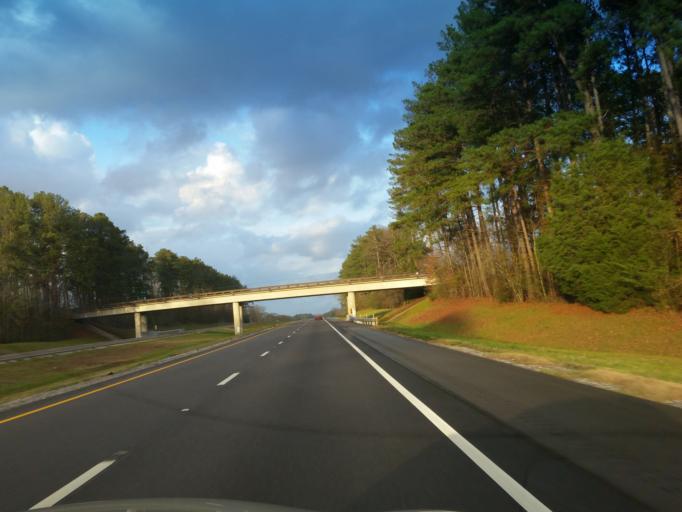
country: US
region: Mississippi
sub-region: Jones County
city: Sharon
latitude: 31.9298
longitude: -88.9985
